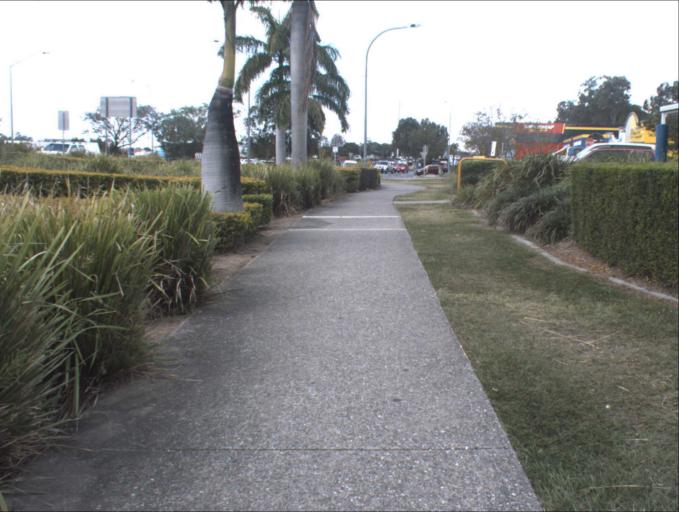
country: AU
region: Queensland
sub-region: Brisbane
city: Sunnybank Hills
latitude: -27.6642
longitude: 153.0364
